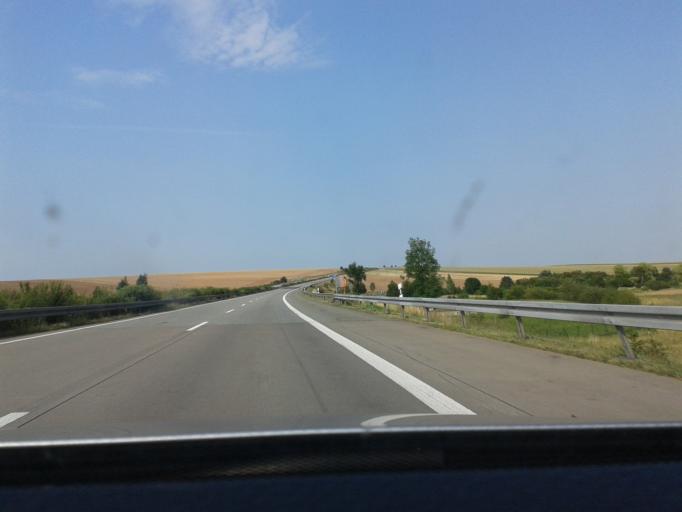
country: DE
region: Thuringia
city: Wipperdorf
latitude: 51.4801
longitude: 10.6967
